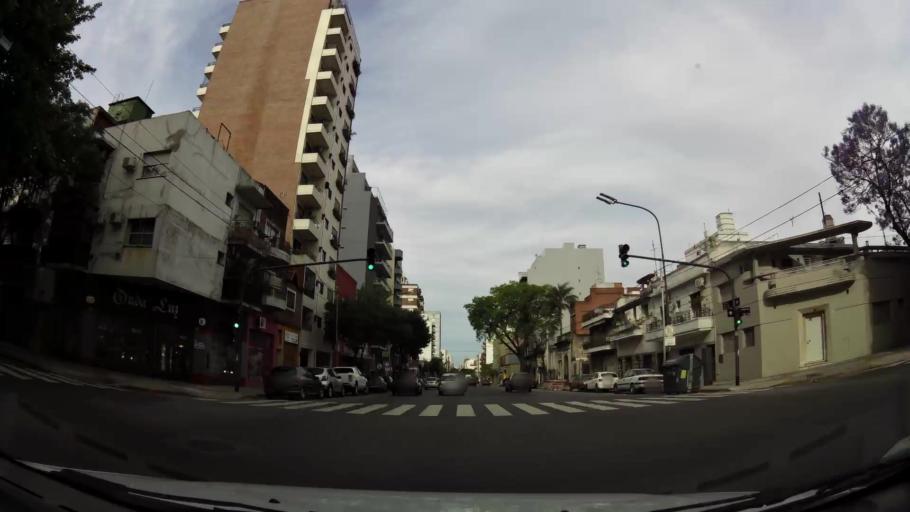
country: AR
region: Buenos Aires F.D.
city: Villa Santa Rita
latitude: -34.6370
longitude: -58.4724
